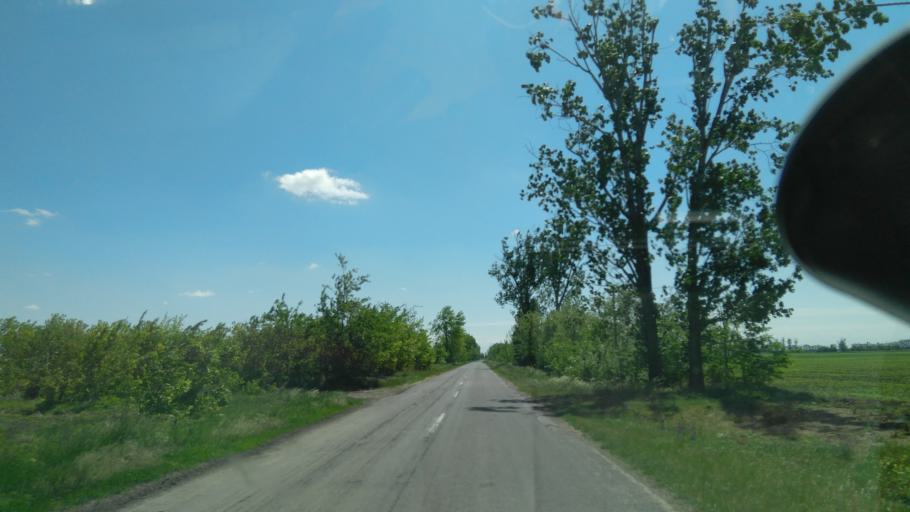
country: HU
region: Bekes
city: Kunagota
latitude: 46.4131
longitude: 21.0468
